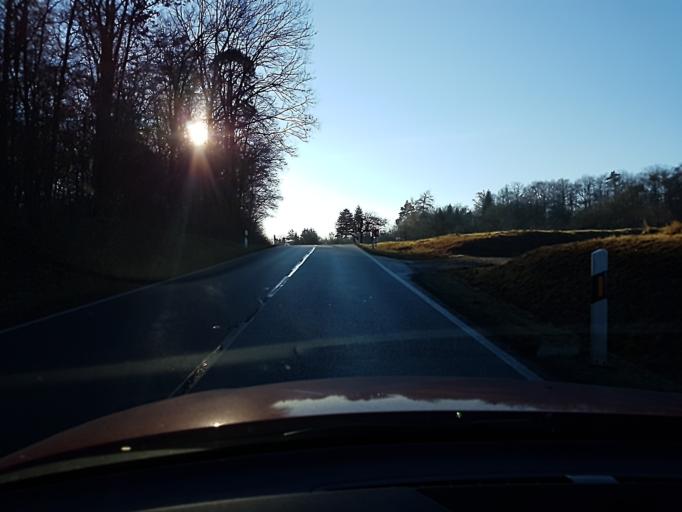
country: DE
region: Baden-Wuerttemberg
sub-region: Regierungsbezirk Stuttgart
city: Sersheim
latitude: 48.9901
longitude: 9.0063
